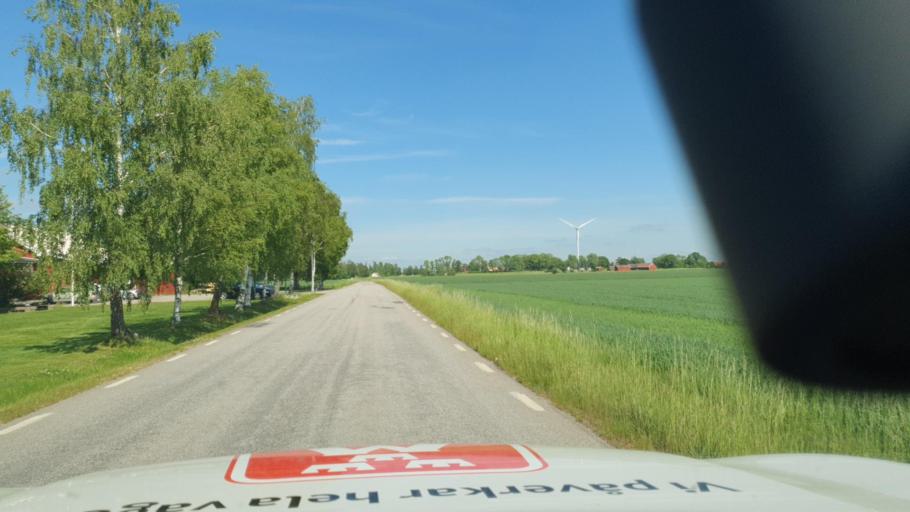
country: SE
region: Vaestra Goetaland
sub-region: Grastorps Kommun
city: Graestorp
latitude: 58.2899
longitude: 12.7518
